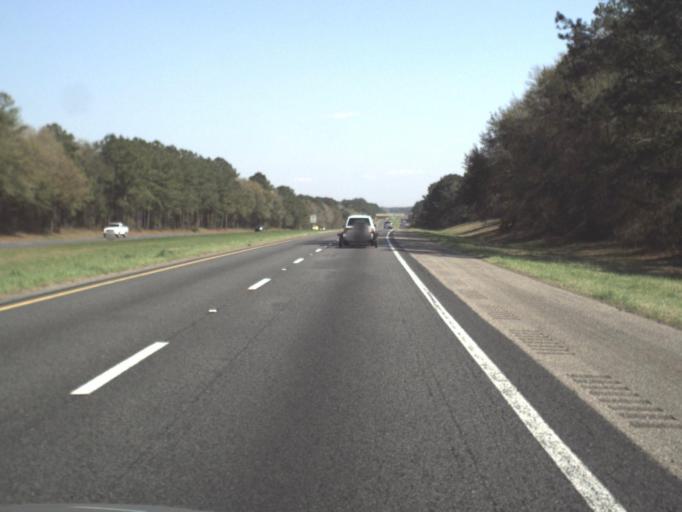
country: US
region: Florida
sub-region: Gadsden County
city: Gretna
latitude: 30.5617
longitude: -84.6454
